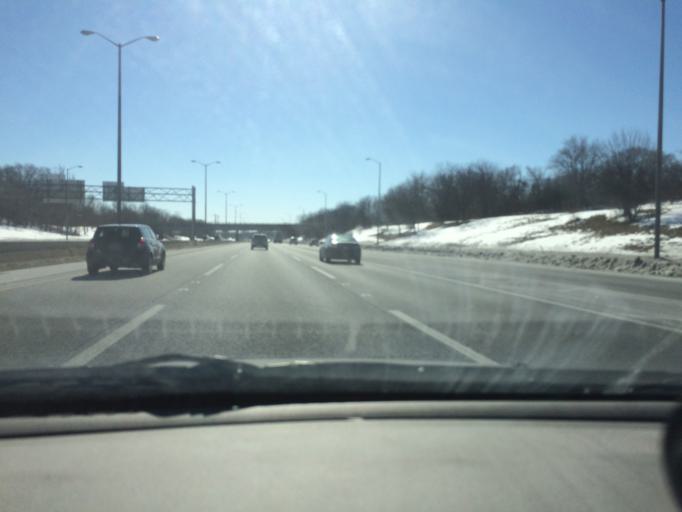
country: US
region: Illinois
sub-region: DuPage County
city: Glendale Heights
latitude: 41.9002
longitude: -88.0380
